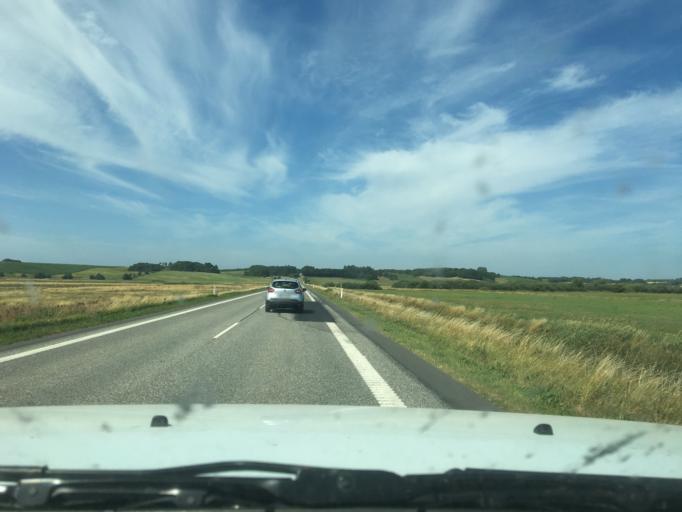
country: DK
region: Central Jutland
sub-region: Viborg Kommune
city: Viborg
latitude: 56.5350
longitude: 9.4035
